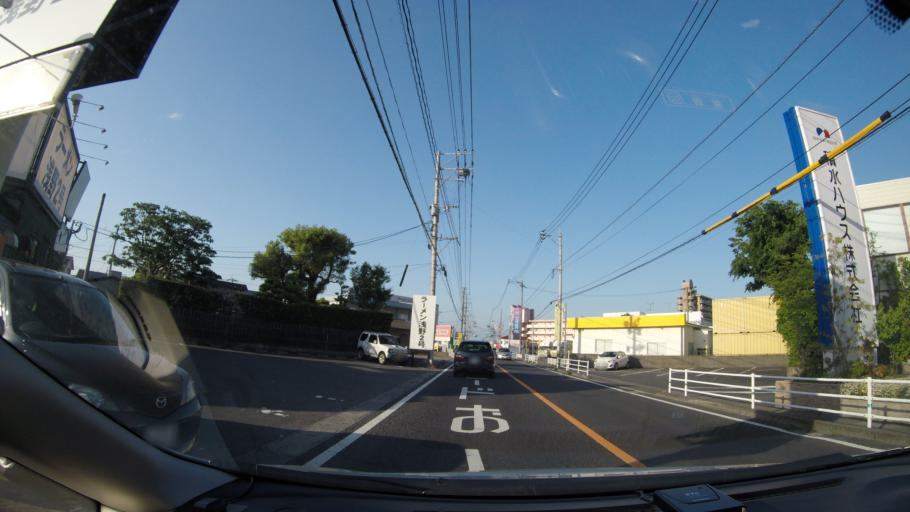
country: JP
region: Oita
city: Oita
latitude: 33.2098
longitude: 131.6062
